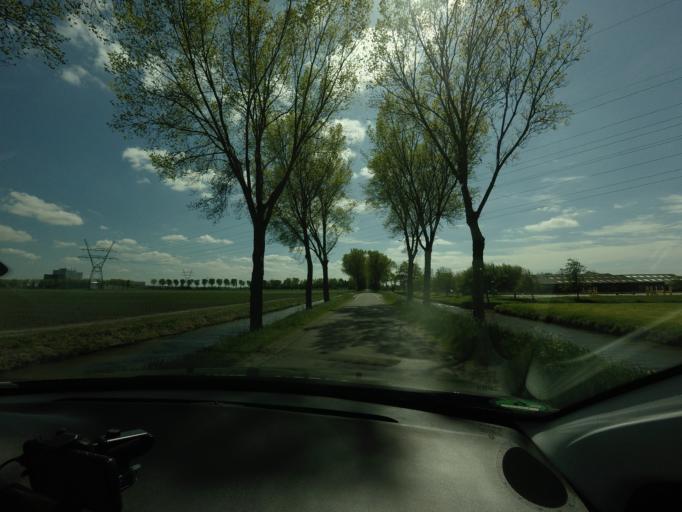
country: NL
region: North Holland
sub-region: Gemeente Beemster
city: Halfweg
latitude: 52.5604
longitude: 4.8709
